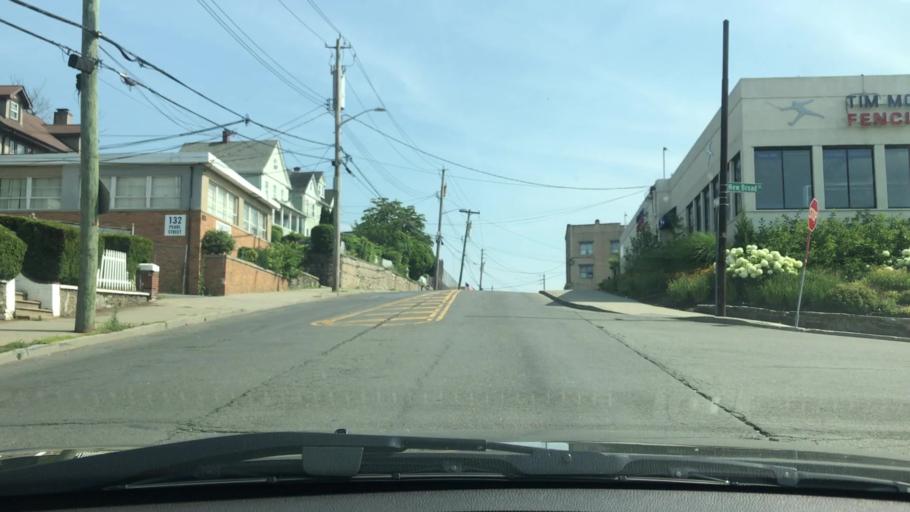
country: US
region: New York
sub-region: Westchester County
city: Port Chester
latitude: 40.9976
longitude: -73.6685
